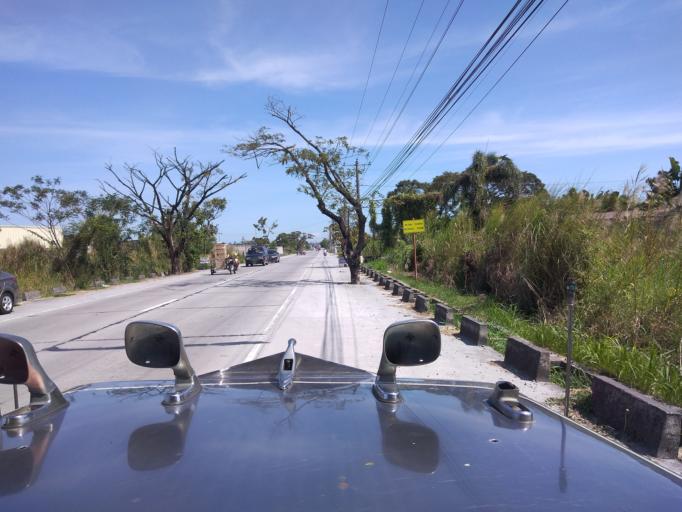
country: PH
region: Central Luzon
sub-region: Province of Pampanga
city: San Juan
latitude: 15.0186
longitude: 120.6702
